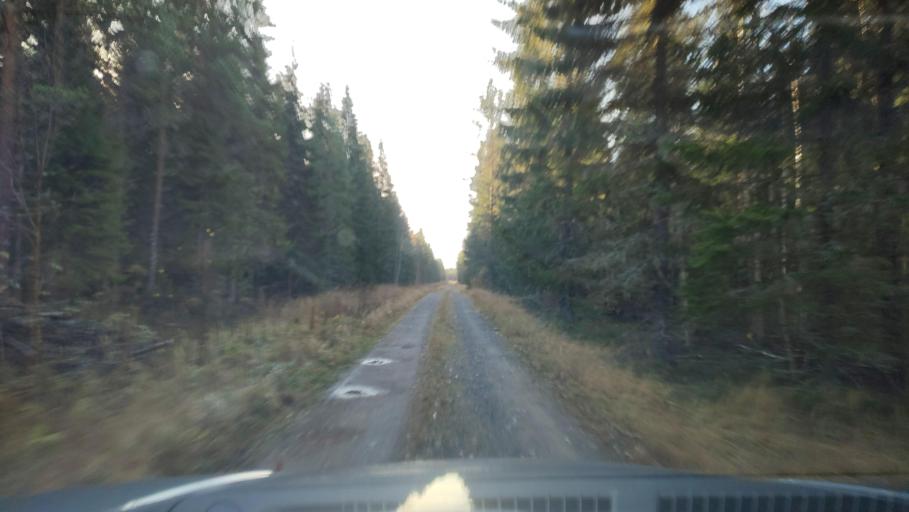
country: FI
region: Southern Ostrobothnia
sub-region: Suupohja
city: Karijoki
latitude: 62.1872
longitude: 21.6076
